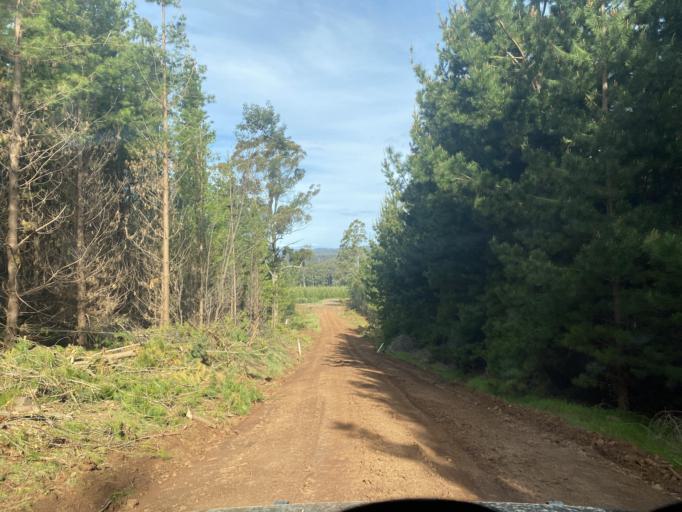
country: AU
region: Victoria
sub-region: Mansfield
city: Mansfield
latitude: -36.8381
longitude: 146.1796
